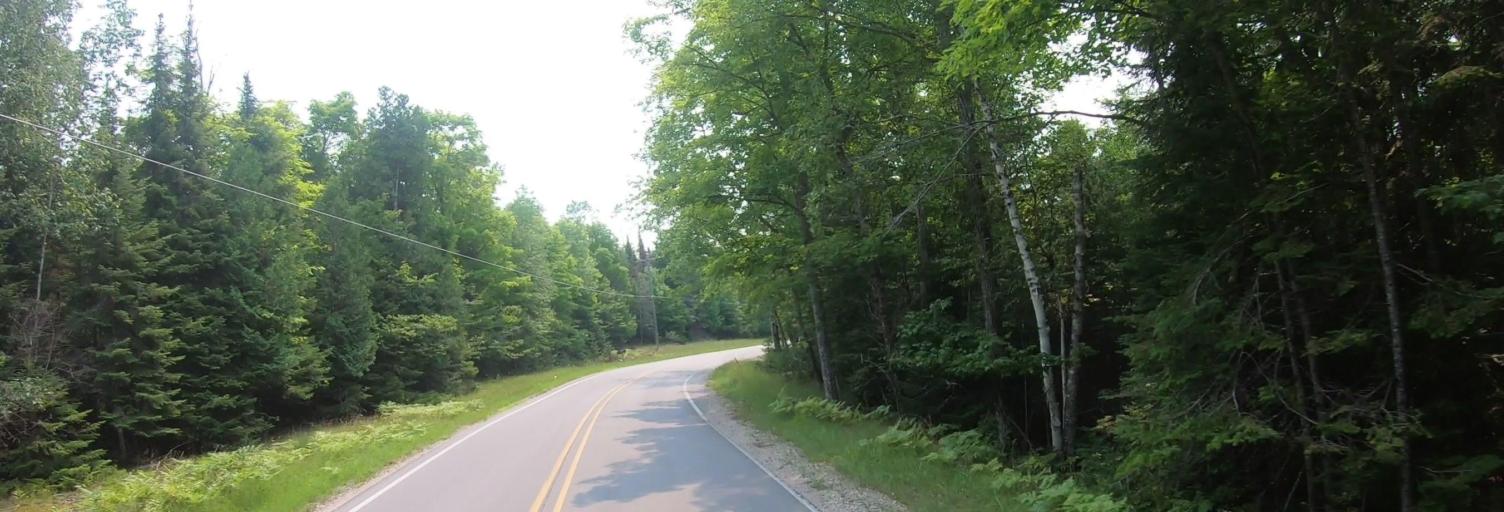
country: CA
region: Ontario
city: Thessalon
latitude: 46.0302
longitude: -83.7289
